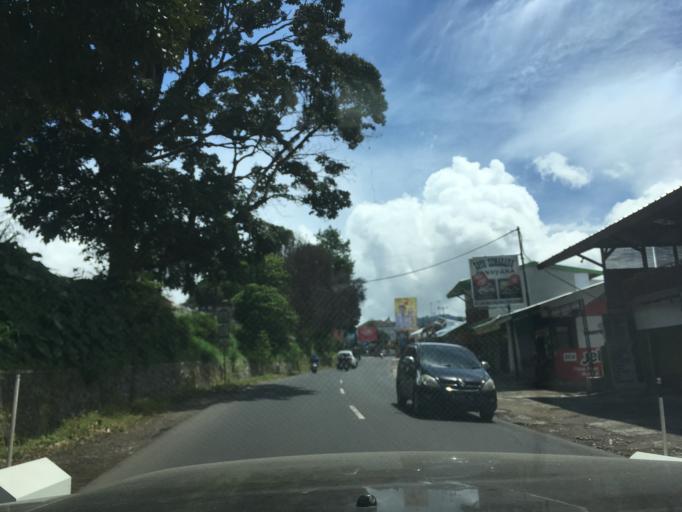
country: ID
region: West Java
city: Lembang
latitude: -6.8045
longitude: 107.6491
